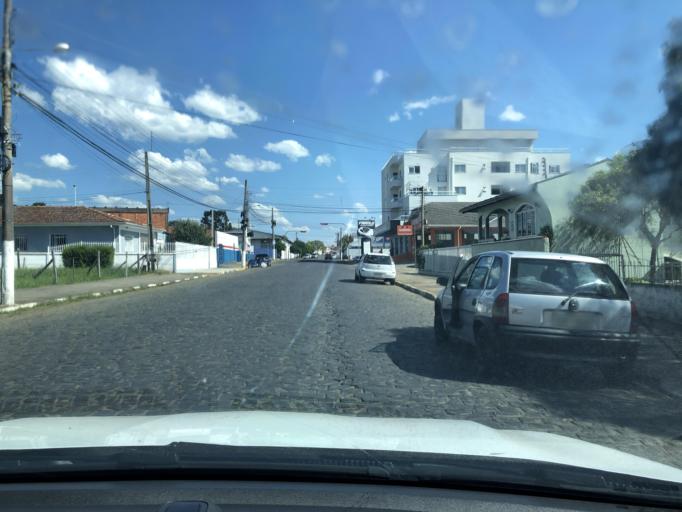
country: BR
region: Santa Catarina
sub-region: Lages
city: Lages
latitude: -27.8151
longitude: -50.3088
